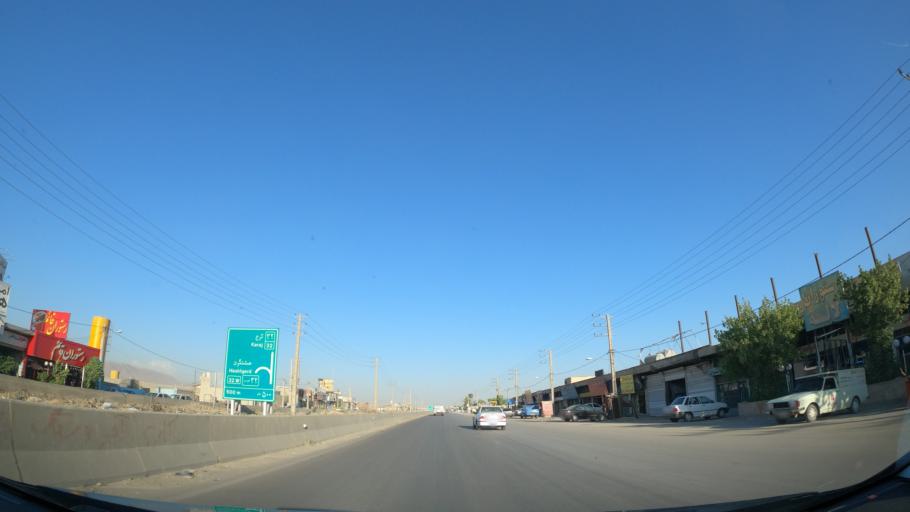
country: IR
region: Alborz
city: Hashtgerd
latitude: 35.9169
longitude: 50.7549
